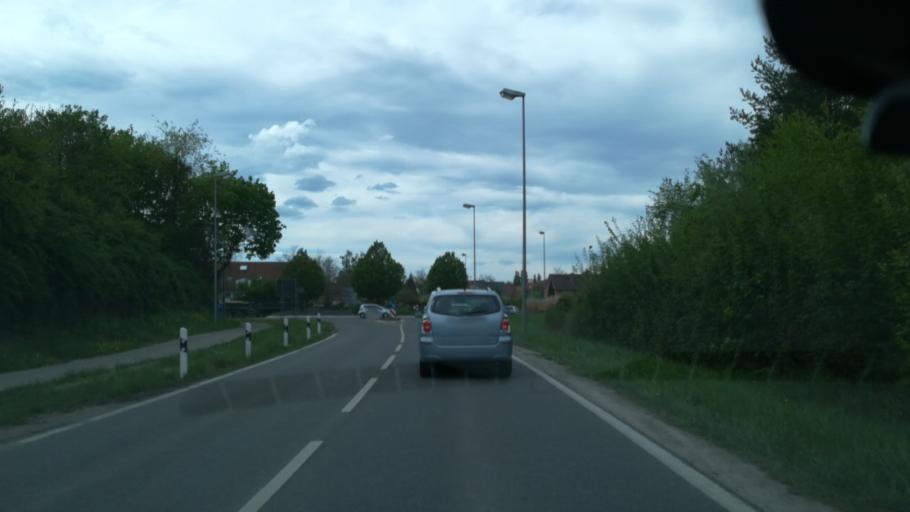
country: DE
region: Baden-Wuerttemberg
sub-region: Freiburg Region
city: Radolfzell am Bodensee
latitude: 47.7500
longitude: 8.9773
